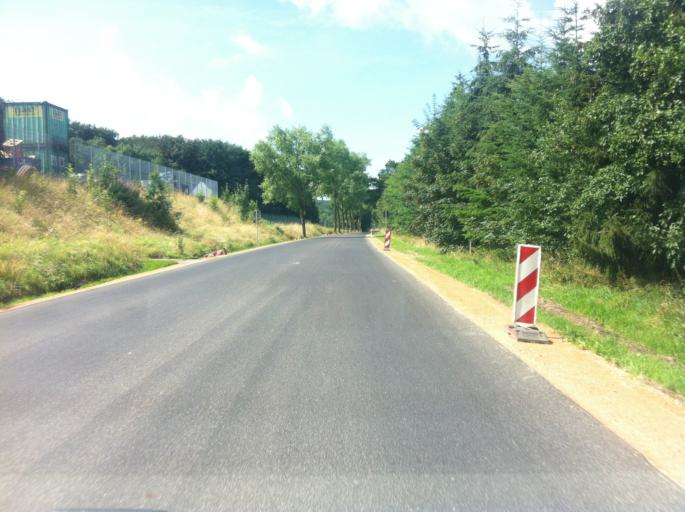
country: DE
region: North Rhine-Westphalia
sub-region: Regierungsbezirk Koln
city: Blankenheim
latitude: 50.4489
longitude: 6.6652
